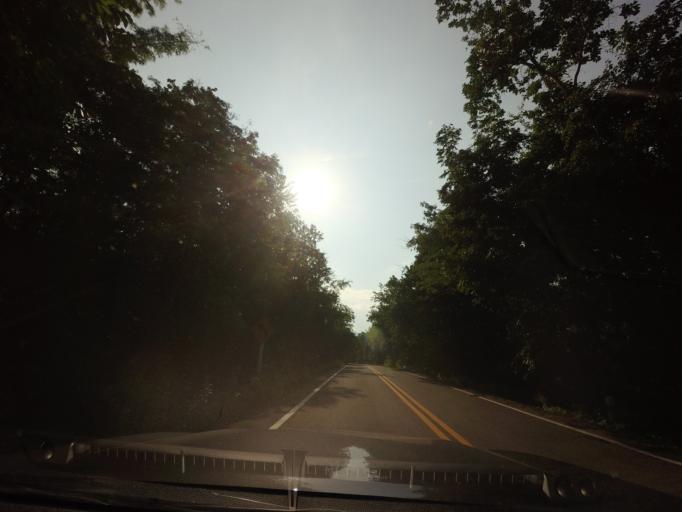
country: TH
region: Nan
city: Na Noi
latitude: 18.3638
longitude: 100.8715
